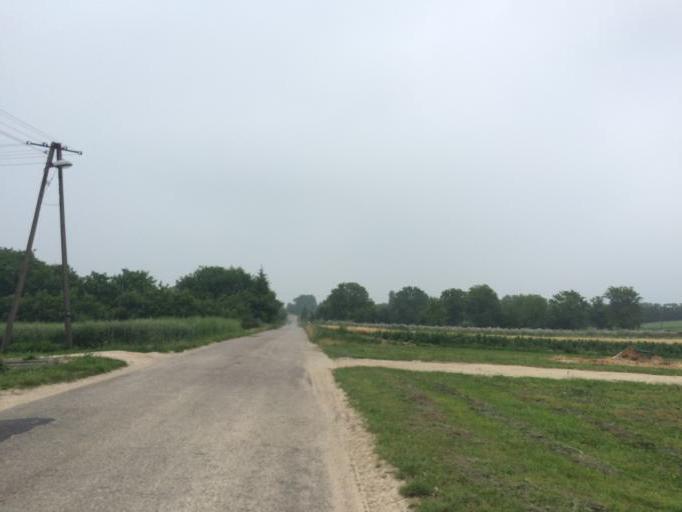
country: PL
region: Lublin Voivodeship
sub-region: Powiat pulawski
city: Markuszow
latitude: 51.3604
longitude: 22.2642
